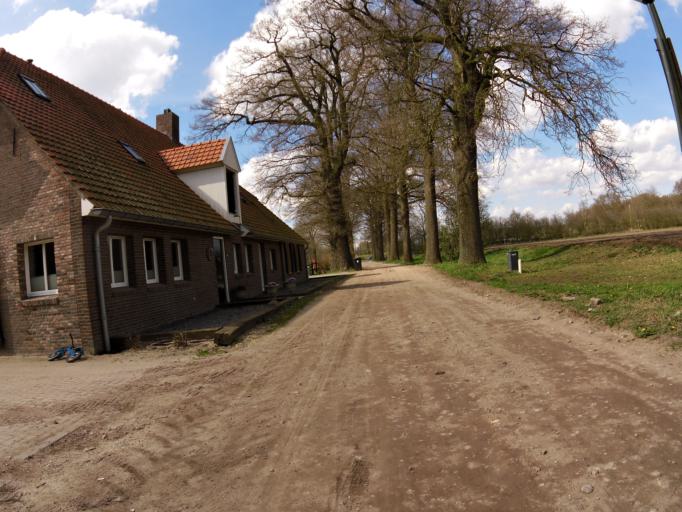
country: NL
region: North Brabant
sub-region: Gemeente Vught
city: Vught
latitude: 51.6417
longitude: 5.2584
